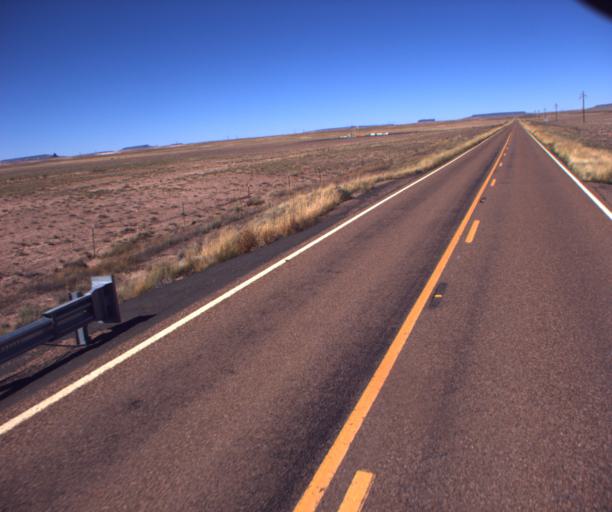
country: US
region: Arizona
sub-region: Navajo County
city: Holbrook
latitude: 35.1063
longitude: -110.0949
